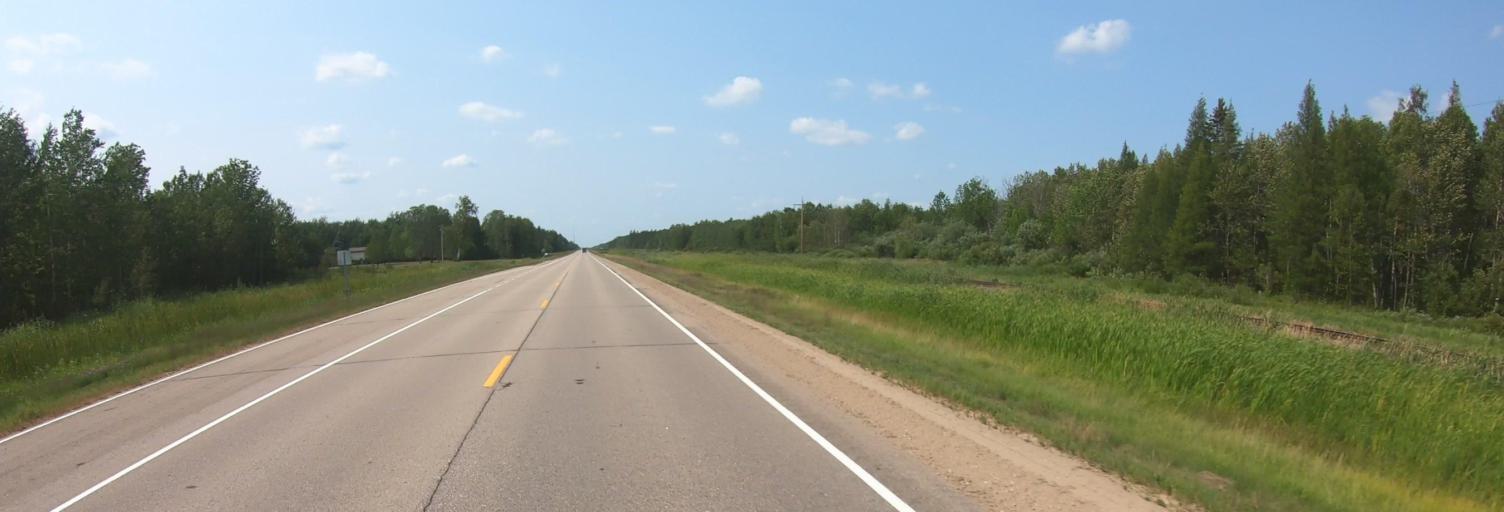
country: US
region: Minnesota
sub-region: Roseau County
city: Warroad
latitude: 48.7785
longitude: -95.0027
